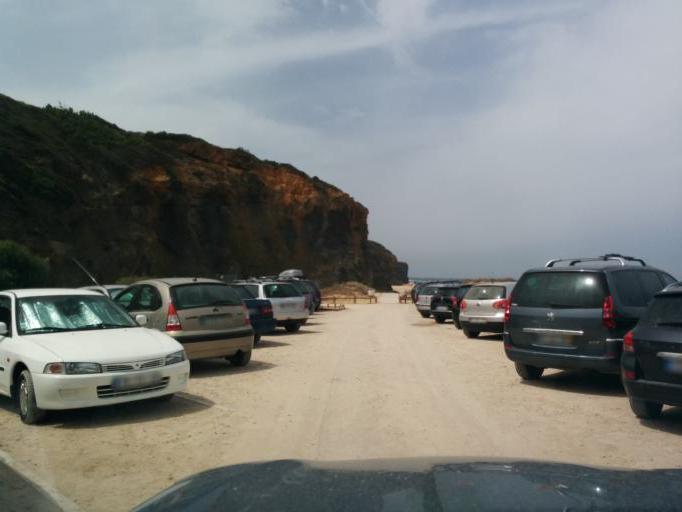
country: PT
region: Beja
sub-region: Odemira
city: Vila Nova de Milfontes
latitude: 37.7143
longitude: -8.7851
